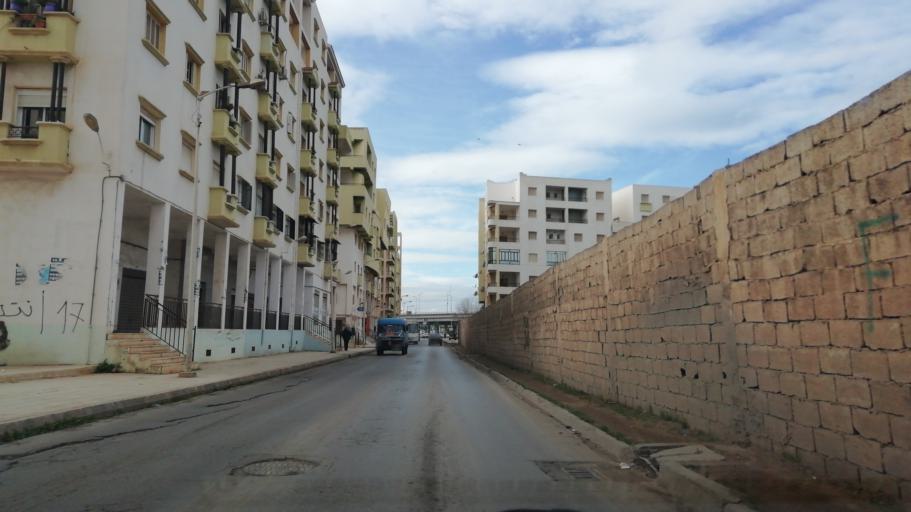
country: DZ
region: Oran
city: Oran
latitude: 35.6848
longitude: -0.6074
